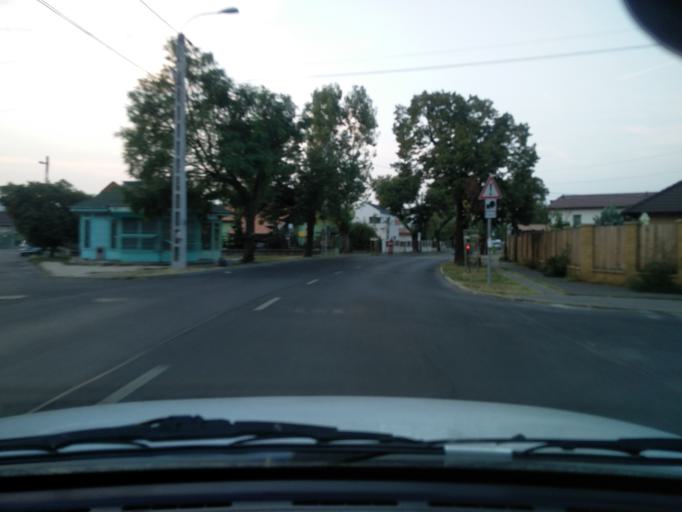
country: HU
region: Budapest
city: Budapest XXIII. keruelet
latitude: 47.4053
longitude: 19.0907
